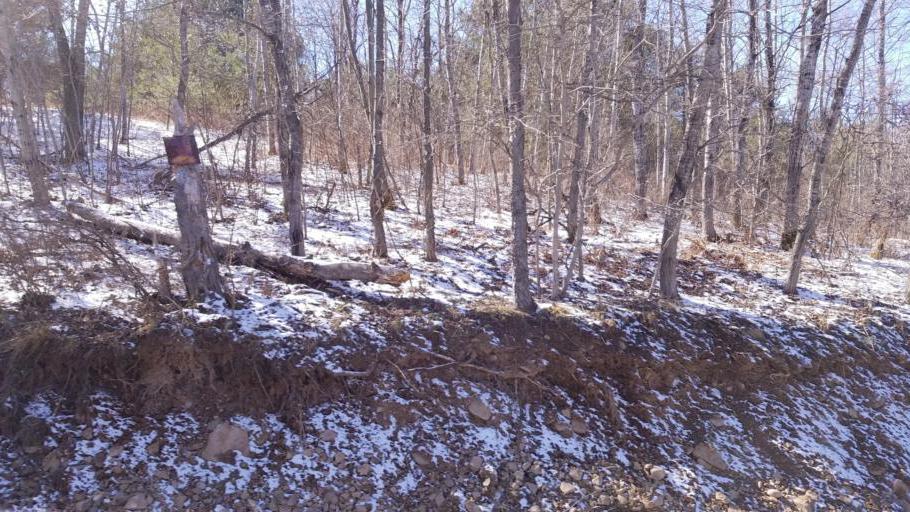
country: US
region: New York
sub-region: Allegany County
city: Wellsville
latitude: 41.9739
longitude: -77.8544
